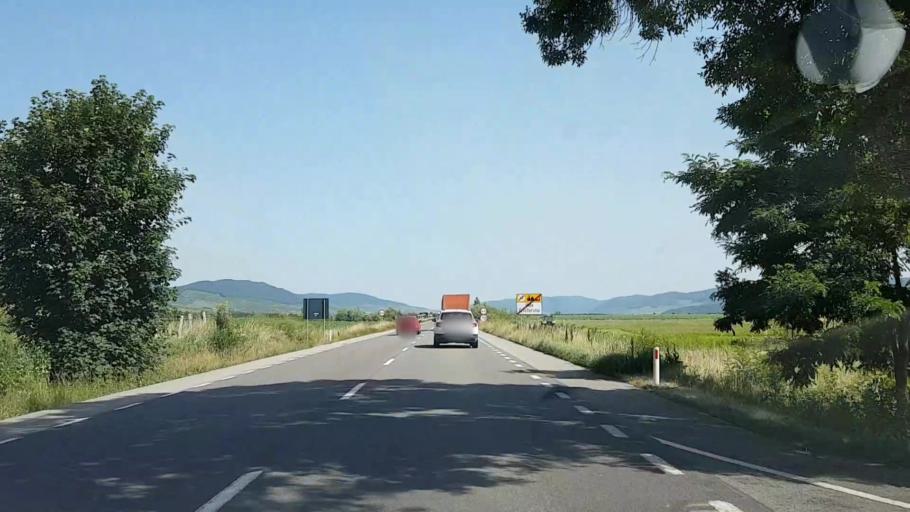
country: RO
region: Bistrita-Nasaud
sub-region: Comuna Sieu-Odorhei
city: Sieu-Odorhei
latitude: 47.1276
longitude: 24.3168
